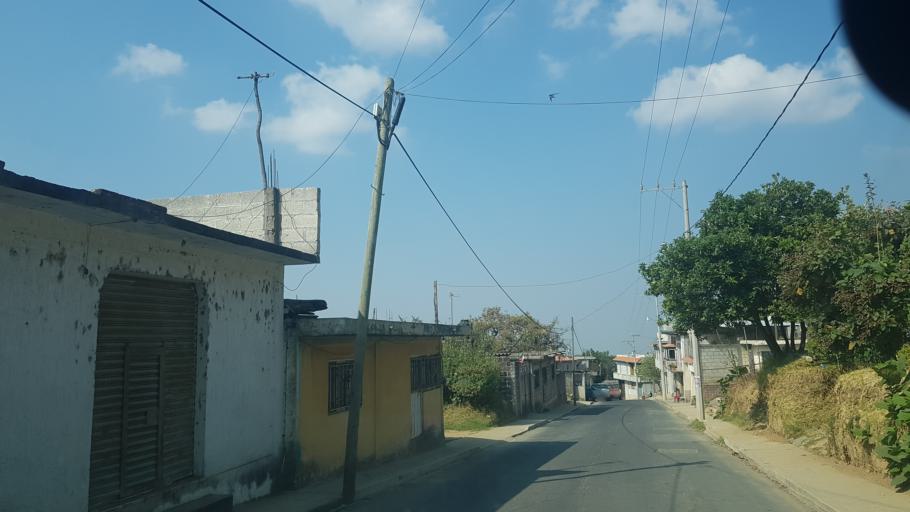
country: MX
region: Morelos
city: Hueyapan
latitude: 18.8917
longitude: -98.6784
